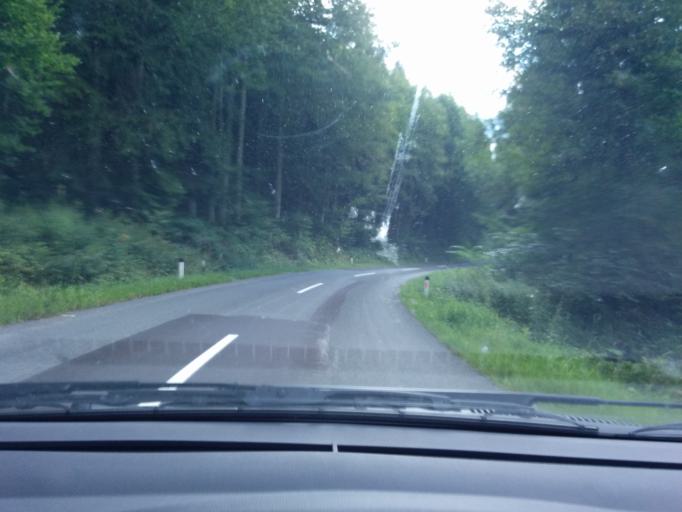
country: AT
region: Upper Austria
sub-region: Politischer Bezirk Rohrbach
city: Ulrichsberg
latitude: 48.7233
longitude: 13.8951
